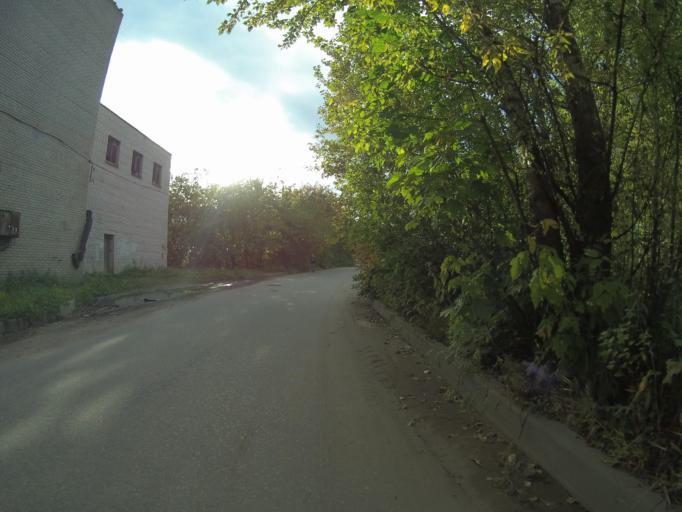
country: RU
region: Vladimir
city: Raduzhnyy
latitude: 56.1047
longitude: 40.2848
